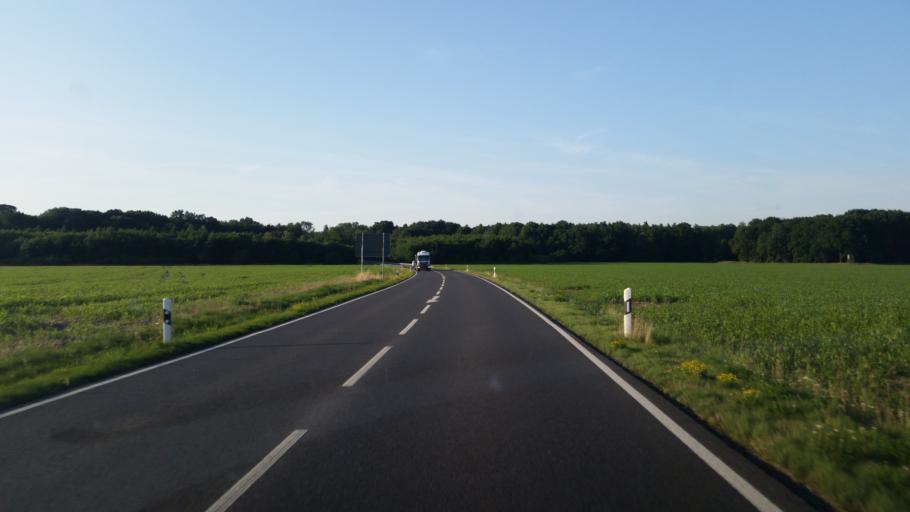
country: DE
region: Saxony
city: Bernsdorf
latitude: 51.3548
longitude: 14.0793
